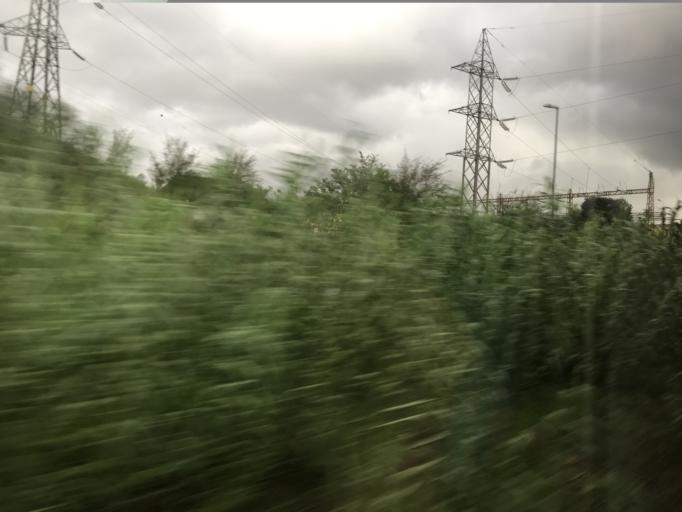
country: IT
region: Latium
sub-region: Citta metropolitana di Roma Capitale
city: Vitinia
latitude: 41.8339
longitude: 12.4406
